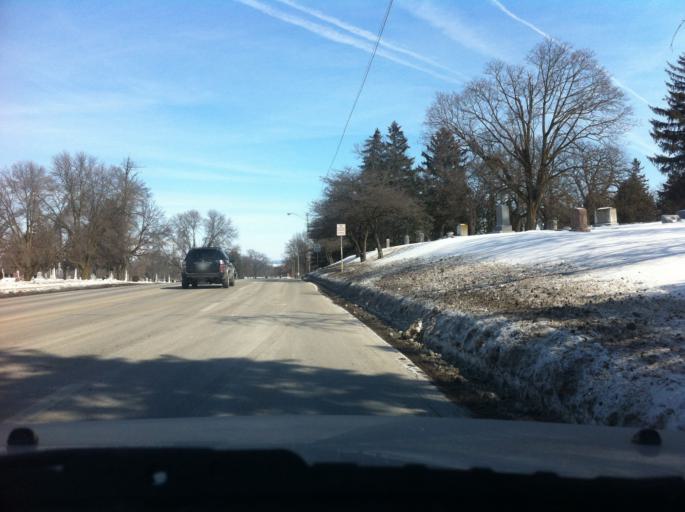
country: US
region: Wisconsin
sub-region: Dane County
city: Shorewood Hills
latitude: 43.0607
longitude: -89.4390
